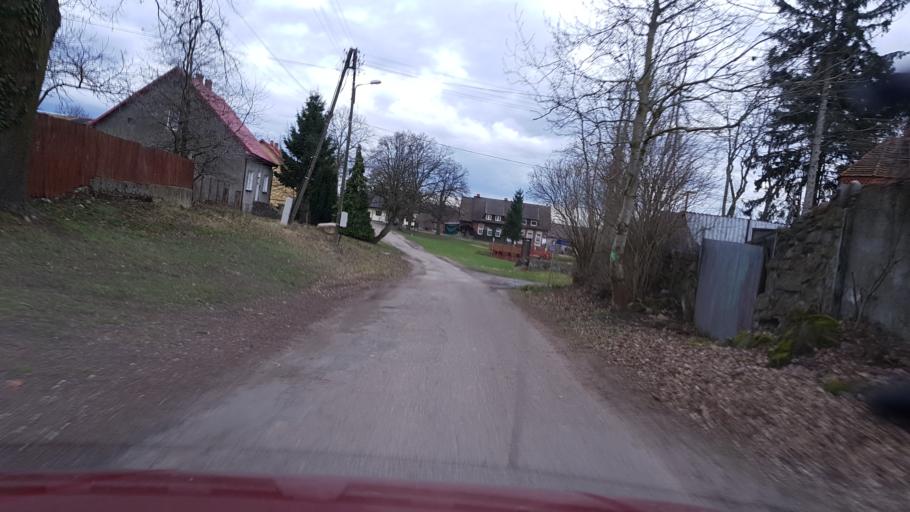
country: PL
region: West Pomeranian Voivodeship
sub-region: Powiat gryfinski
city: Stare Czarnowo
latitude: 53.3258
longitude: 14.6816
